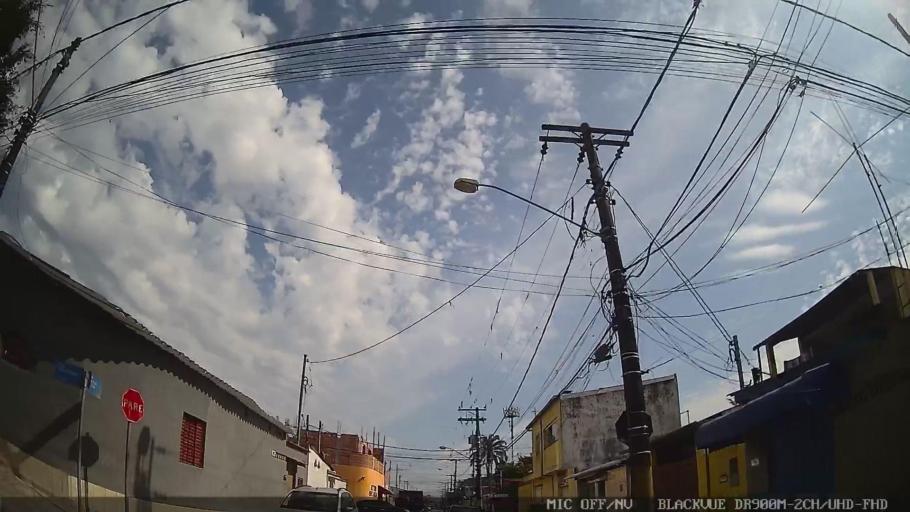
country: BR
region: Sao Paulo
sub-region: Santos
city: Santos
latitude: -23.9444
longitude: -46.2867
